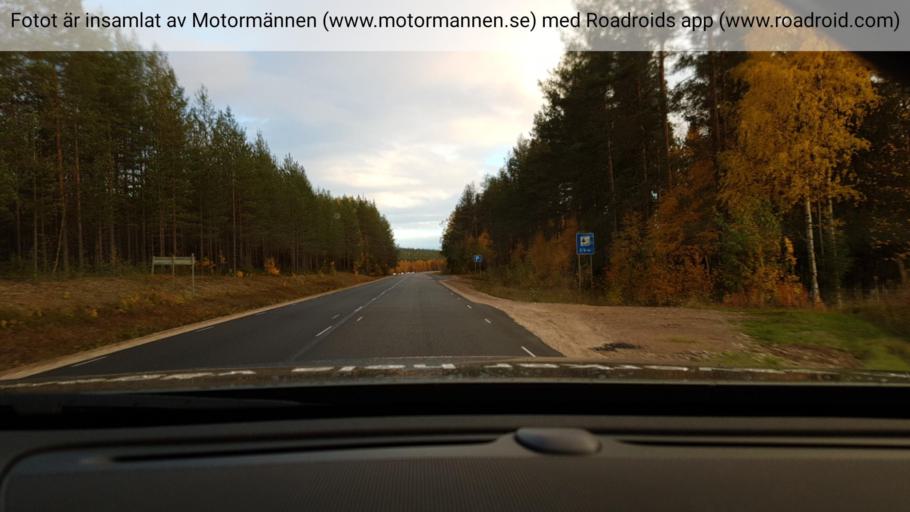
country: SE
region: Norrbotten
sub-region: Overkalix Kommun
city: OEverkalix
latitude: 66.4221
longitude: 22.8002
